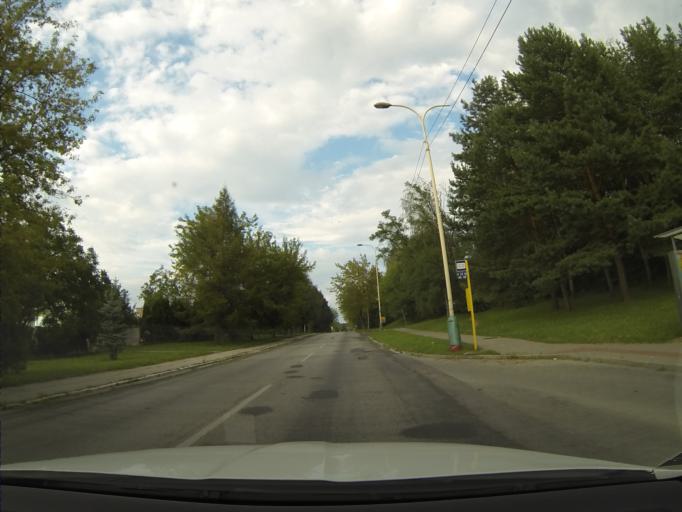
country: SK
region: Nitriansky
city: Prievidza
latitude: 48.7754
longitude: 18.6405
